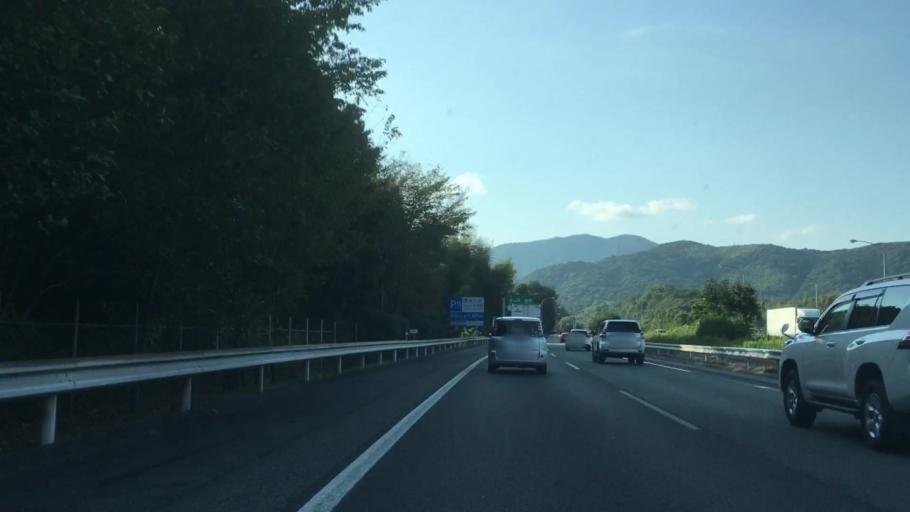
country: JP
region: Yamaguchi
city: Hofu
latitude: 34.0676
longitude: 131.6895
